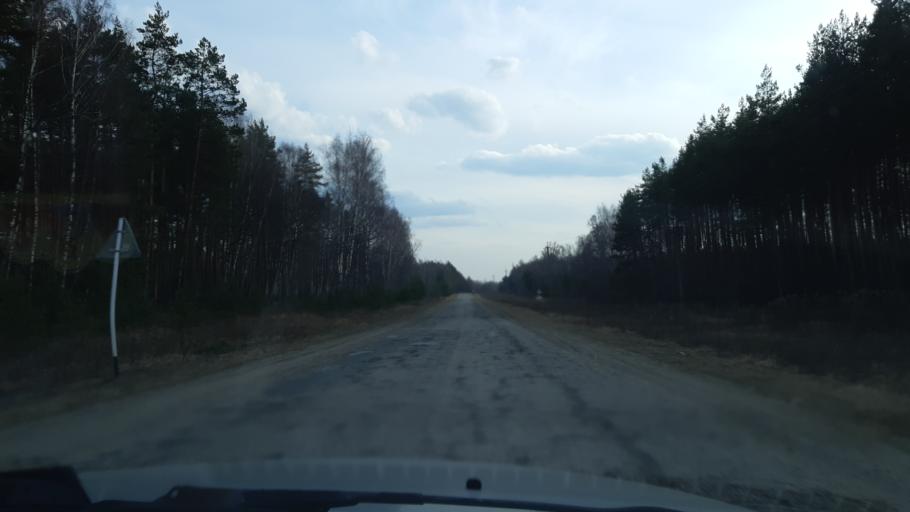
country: RU
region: Vladimir
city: Nikologory
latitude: 56.1174
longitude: 41.9856
